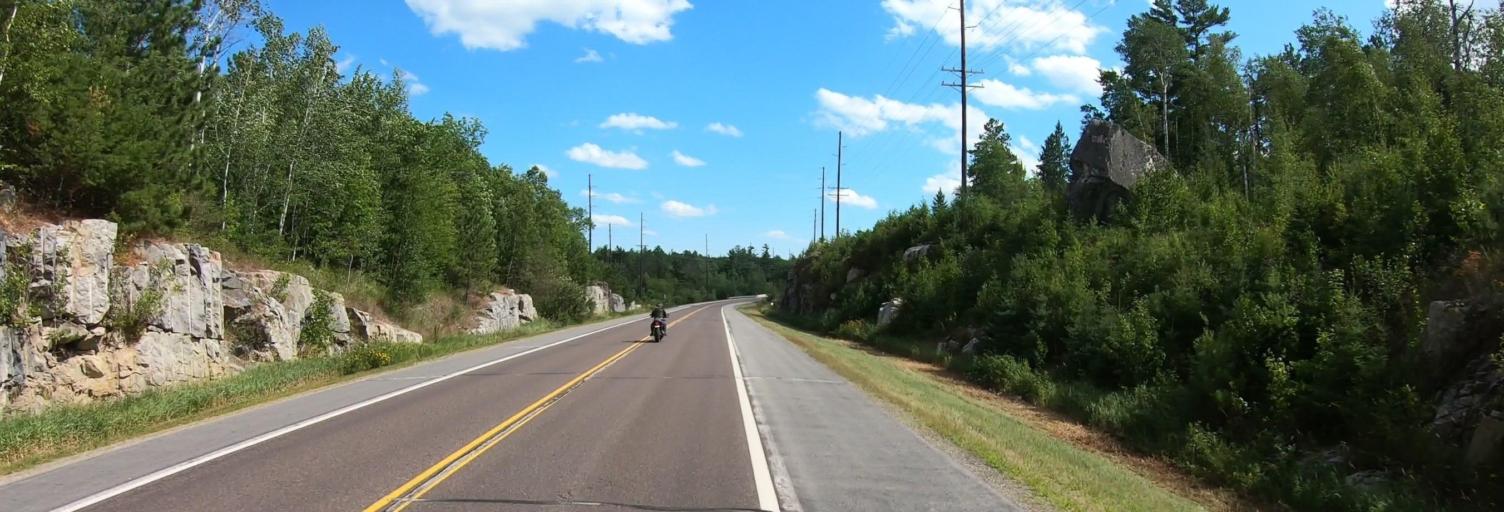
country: US
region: Minnesota
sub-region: Saint Louis County
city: Aurora
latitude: 47.7942
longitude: -92.3708
